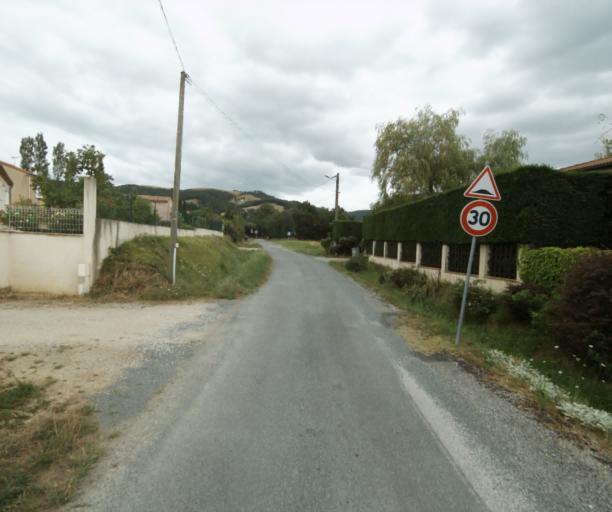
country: FR
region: Midi-Pyrenees
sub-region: Departement du Tarn
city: Soreze
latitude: 43.4582
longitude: 2.0701
